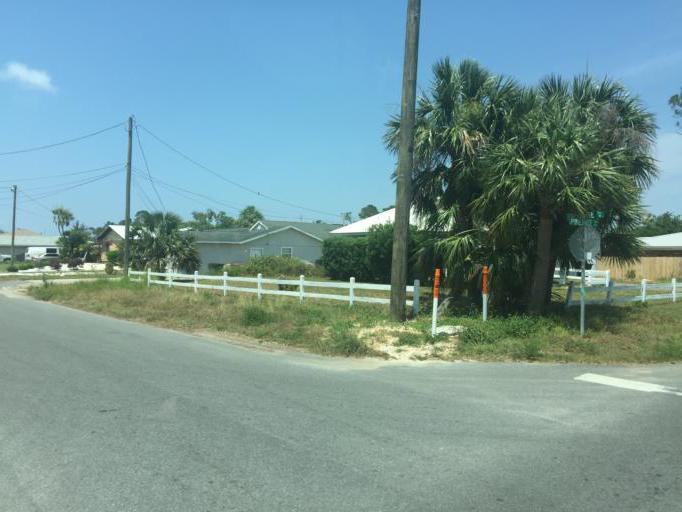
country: US
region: Florida
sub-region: Bay County
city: Lower Grand Lagoon
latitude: 30.1445
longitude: -85.7527
